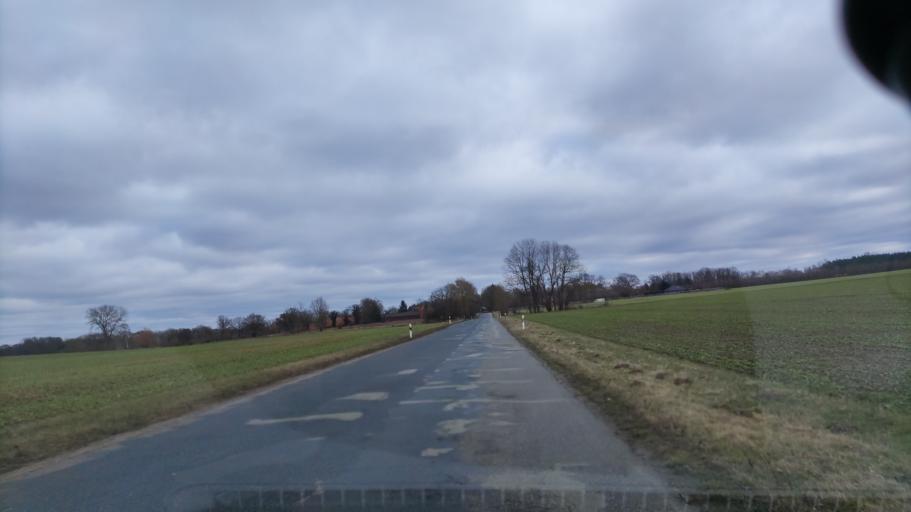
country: DE
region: Lower Saxony
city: Bleckede
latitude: 53.2640
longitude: 10.7342
